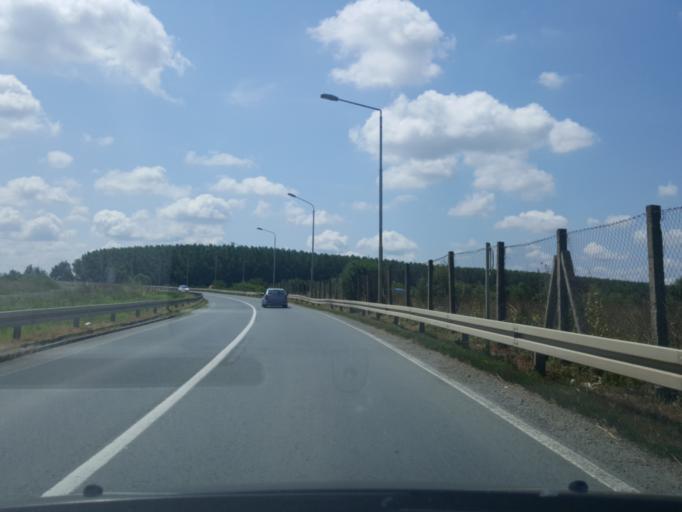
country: RS
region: Autonomna Pokrajina Vojvodina
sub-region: Sremski Okrug
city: Sremska Mitrovica
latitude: 44.9660
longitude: 19.6321
